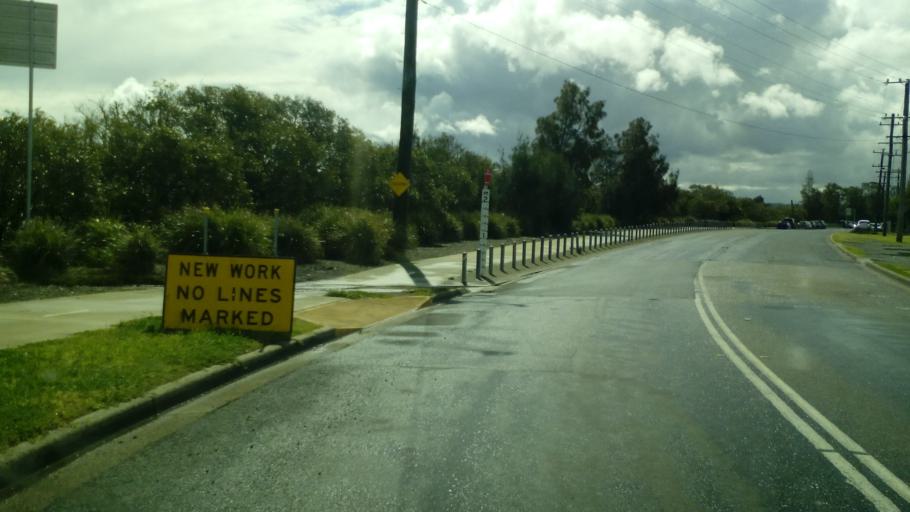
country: AU
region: New South Wales
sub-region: Lake Macquarie Shire
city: Glendale
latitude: -32.9563
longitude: 151.6149
